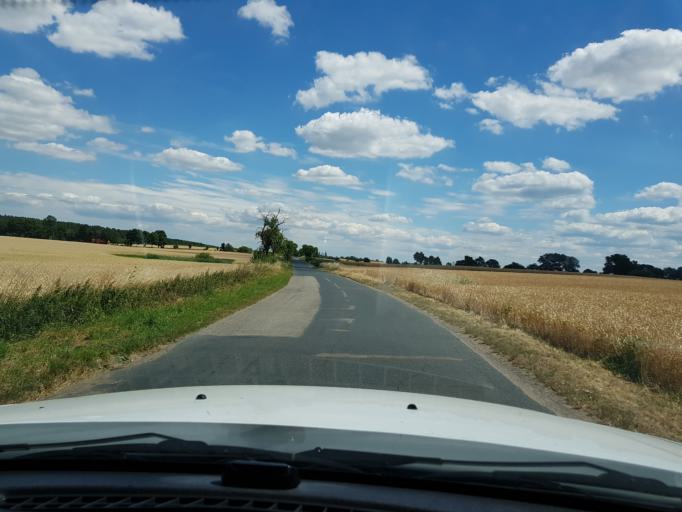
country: PL
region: West Pomeranian Voivodeship
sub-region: Powiat mysliborski
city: Nowogrodek Pomorski
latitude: 52.9090
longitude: 14.9653
